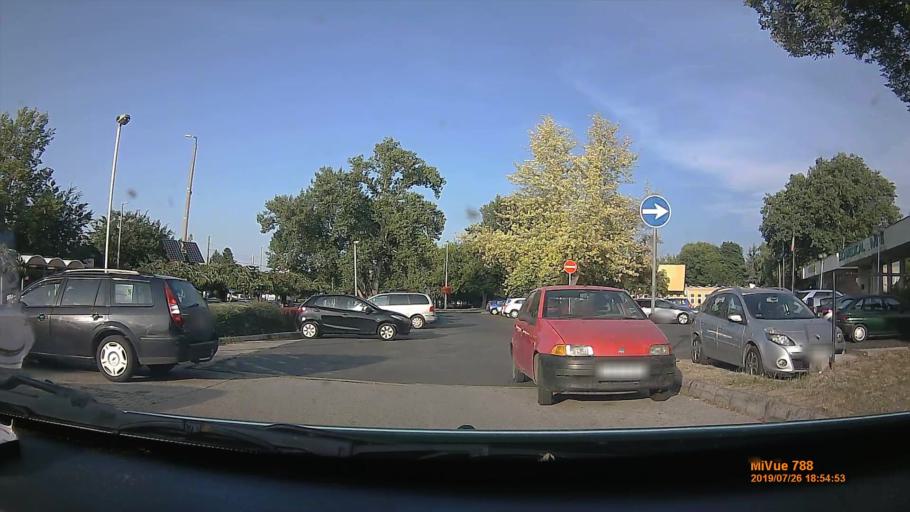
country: HU
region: Somogy
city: Siofok
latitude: 46.9013
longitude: 18.0439
